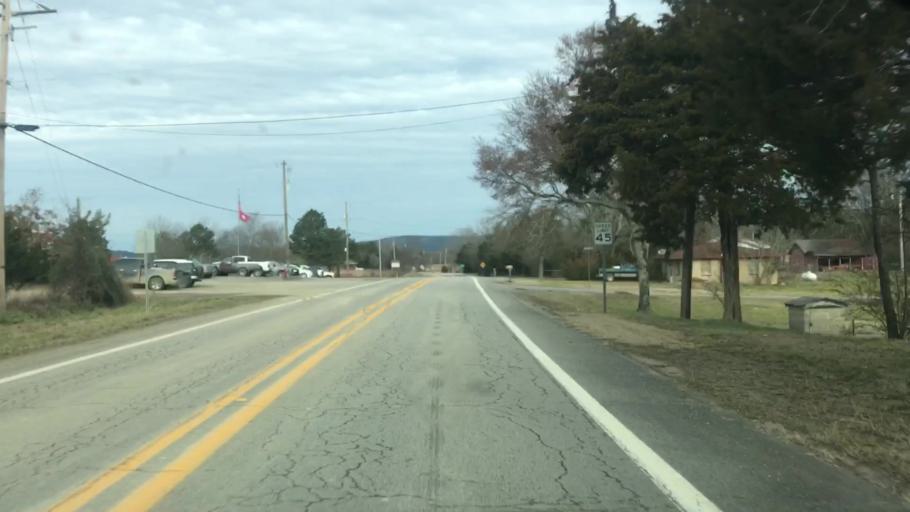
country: US
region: Arkansas
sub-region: Montgomery County
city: Mount Ida
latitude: 34.6312
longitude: -93.7350
